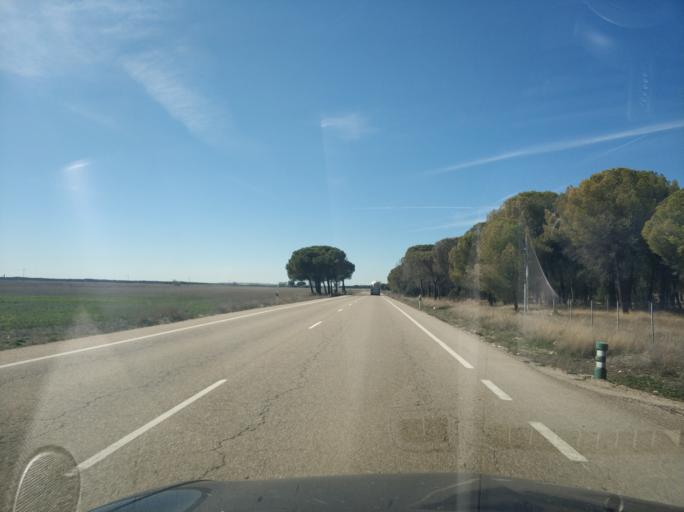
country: ES
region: Castille and Leon
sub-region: Provincia de Valladolid
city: Aldeamayor de San Martin
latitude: 41.5587
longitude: -4.6257
